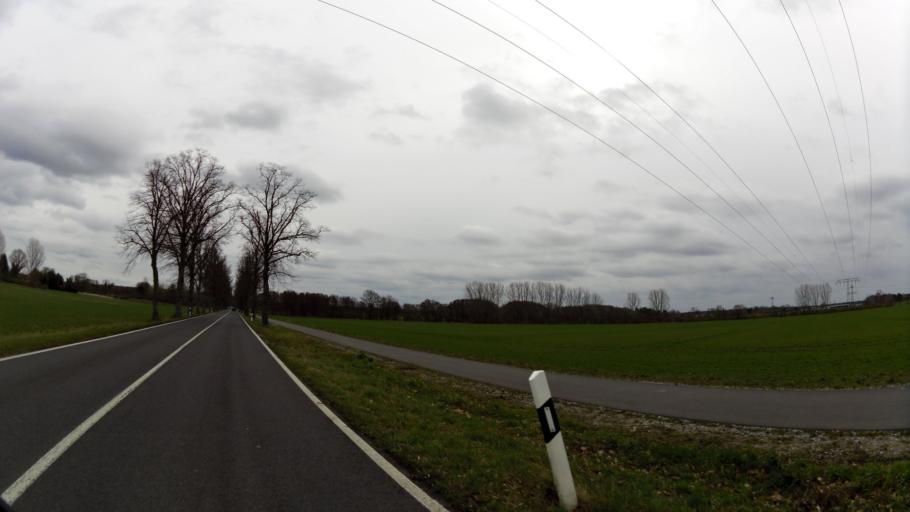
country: DE
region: Brandenburg
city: Schonefeld
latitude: 52.3473
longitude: 13.5398
